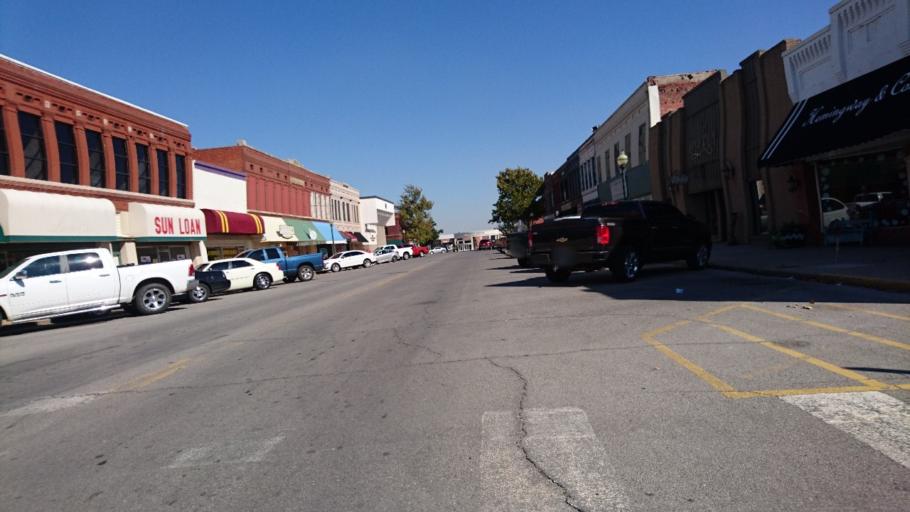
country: US
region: Oklahoma
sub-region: Custer County
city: Clinton
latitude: 35.5144
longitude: -98.9672
